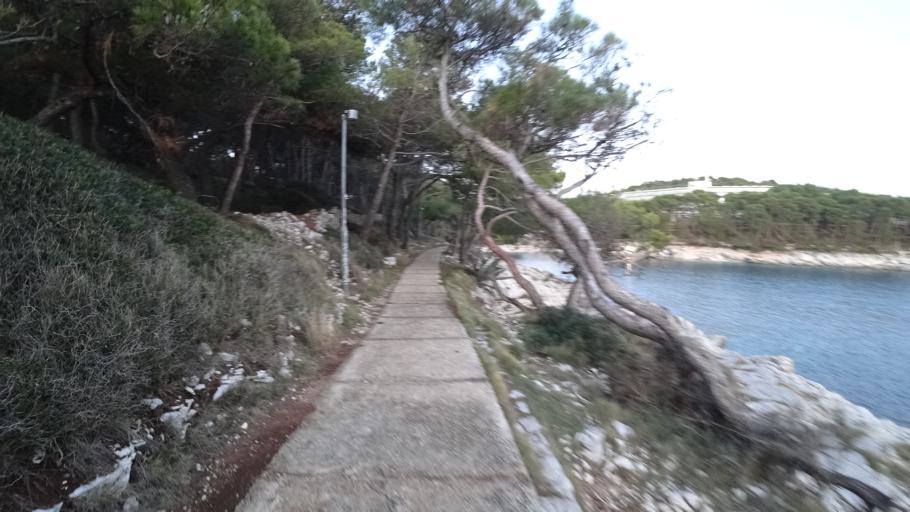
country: HR
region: Primorsko-Goranska
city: Mali Losinj
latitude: 44.5237
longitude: 14.4557
